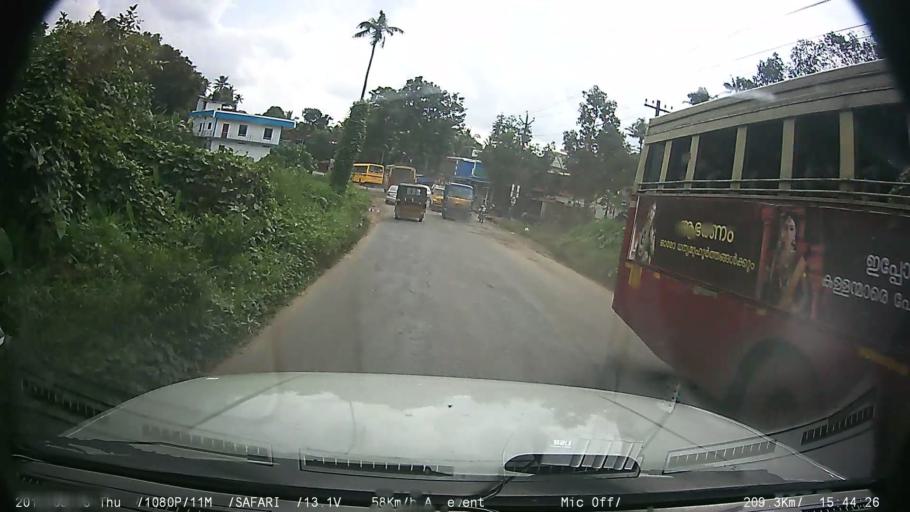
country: IN
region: Kerala
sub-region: Ernakulam
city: Piravam
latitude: 9.8487
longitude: 76.5922
